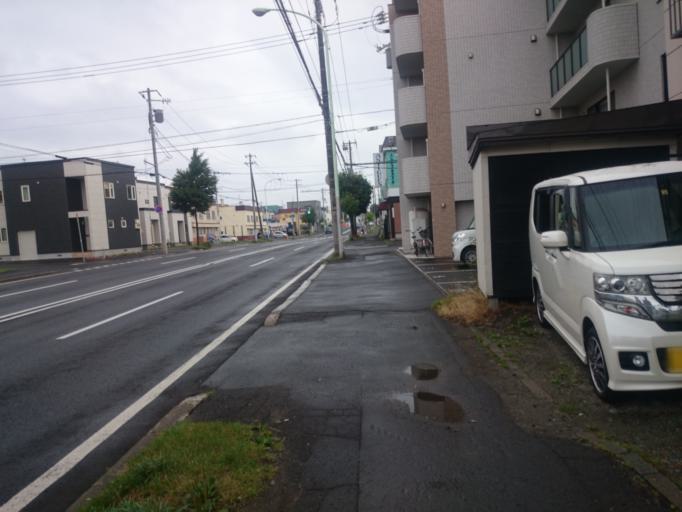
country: JP
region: Hokkaido
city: Sapporo
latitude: 43.0567
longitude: 141.4034
